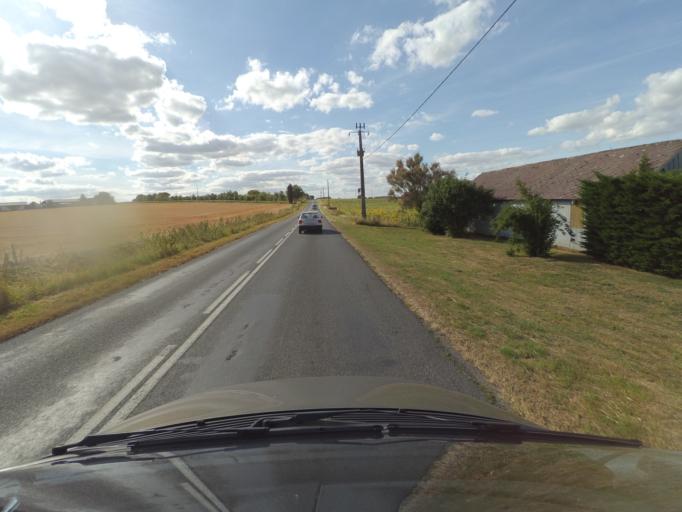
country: FR
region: Poitou-Charentes
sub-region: Departement de la Vienne
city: Saint-Gervais-les-Trois-Clochers
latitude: 46.9519
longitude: 0.4077
